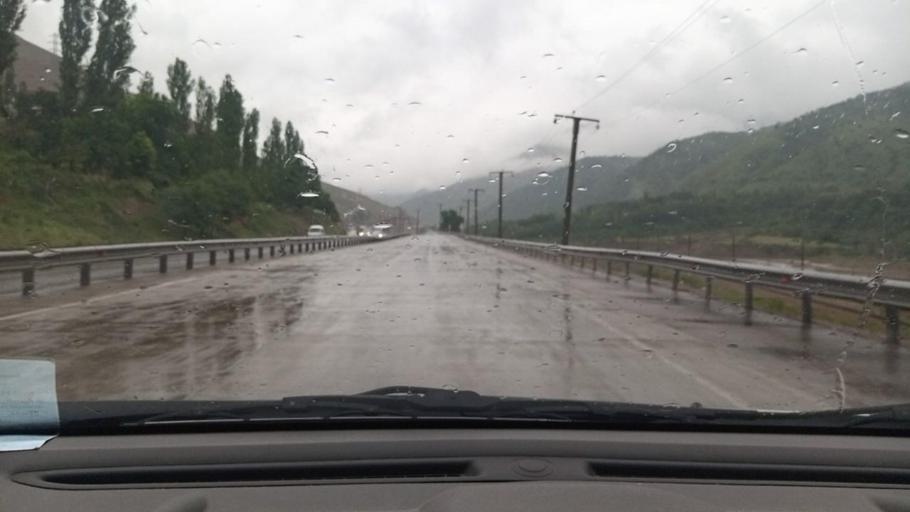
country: UZ
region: Toshkent
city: Angren
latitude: 41.1460
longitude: 70.4094
